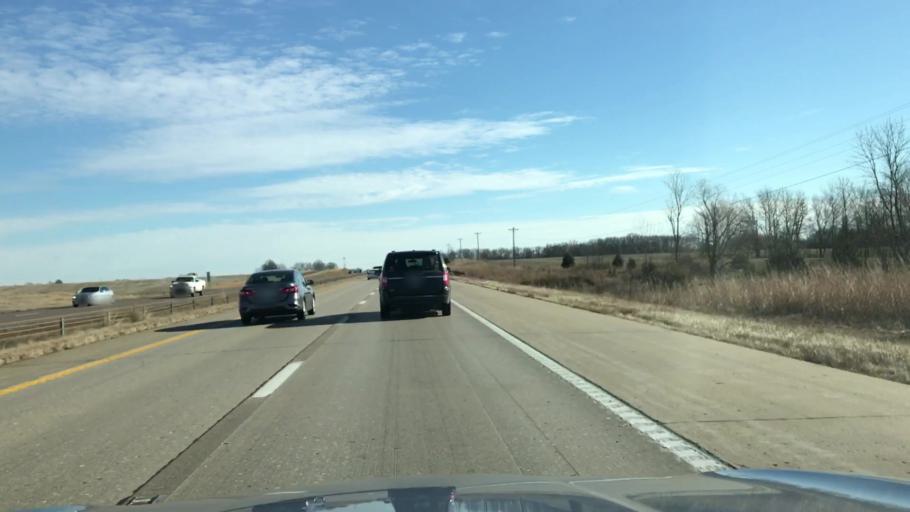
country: US
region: Missouri
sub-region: Callaway County
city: Fulton
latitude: 38.9250
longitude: -91.7736
